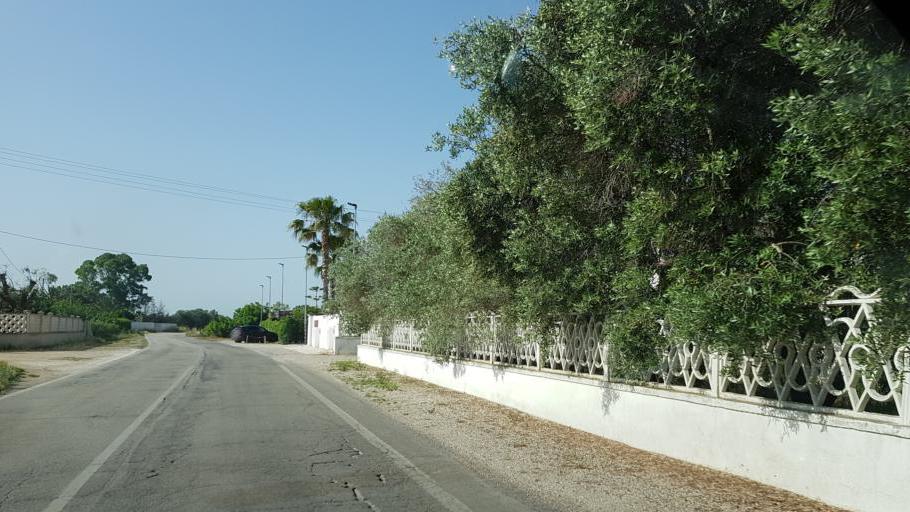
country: IT
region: Apulia
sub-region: Provincia di Brindisi
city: Mesagne
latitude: 40.5342
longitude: 17.8188
